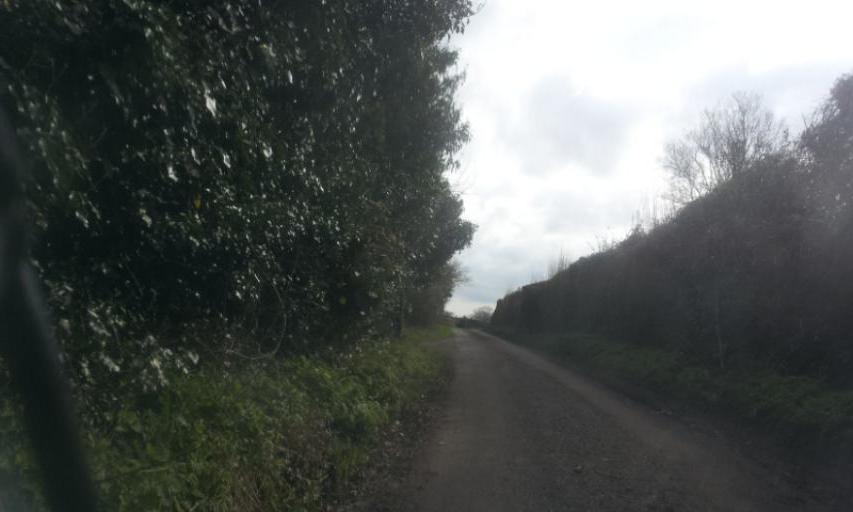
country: GB
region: England
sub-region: Kent
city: Teynham
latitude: 51.3294
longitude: 0.8424
